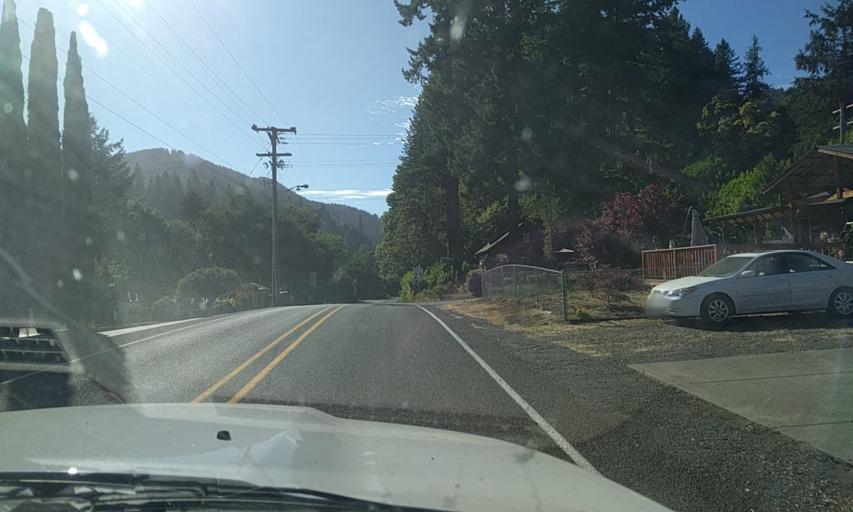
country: US
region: Oregon
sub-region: Lane County
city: Florence
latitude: 44.0361
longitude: -123.8577
